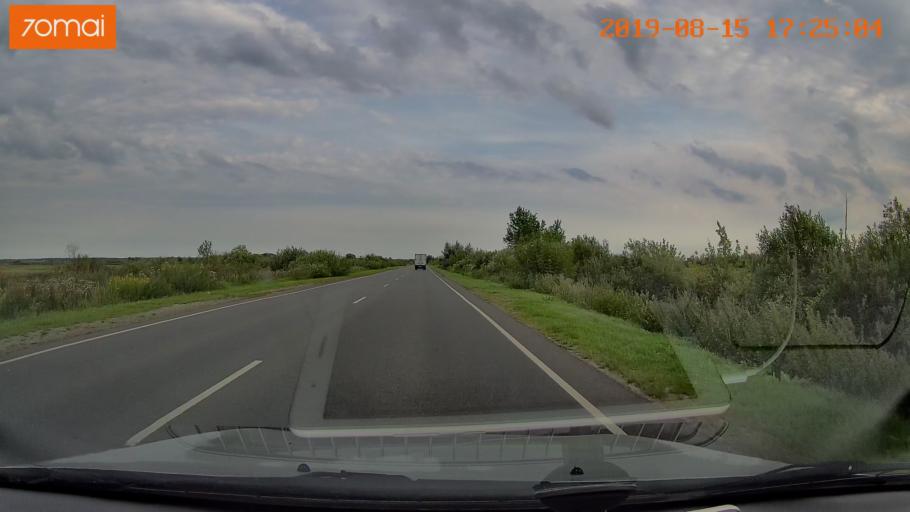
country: RU
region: Moskovskaya
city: Ashitkovo
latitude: 55.3791
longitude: 38.5614
